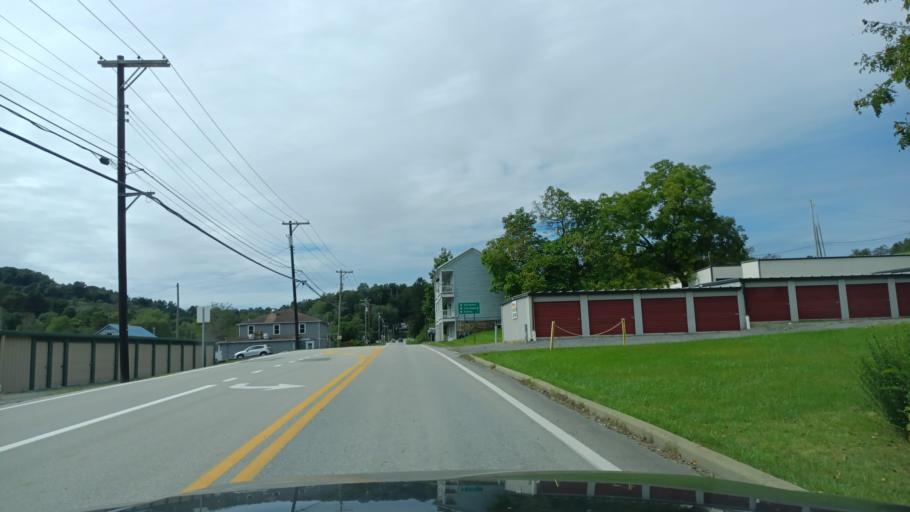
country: US
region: West Virginia
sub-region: Taylor County
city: Grafton
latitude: 39.3339
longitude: -80.0769
